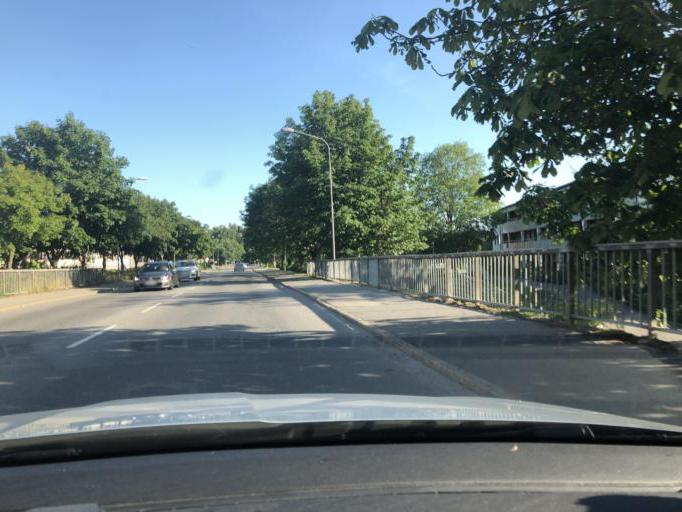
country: SE
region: Stockholm
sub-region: Huddinge Kommun
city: Segeltorp
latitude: 59.2763
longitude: 17.9028
